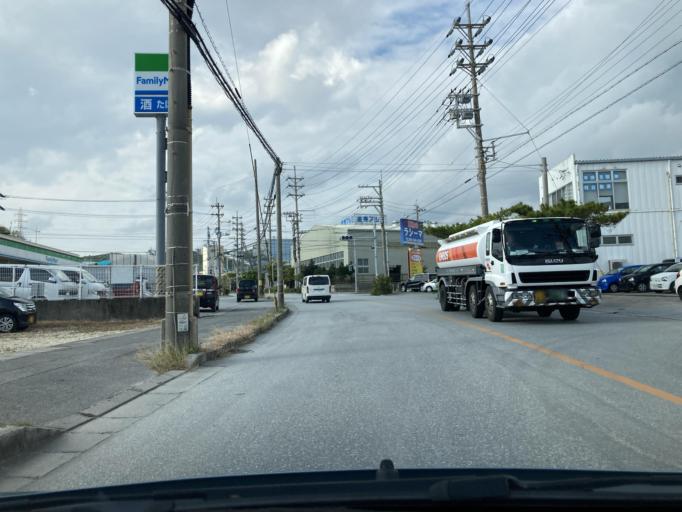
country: JP
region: Okinawa
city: Ginowan
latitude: 26.2304
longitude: 127.7739
